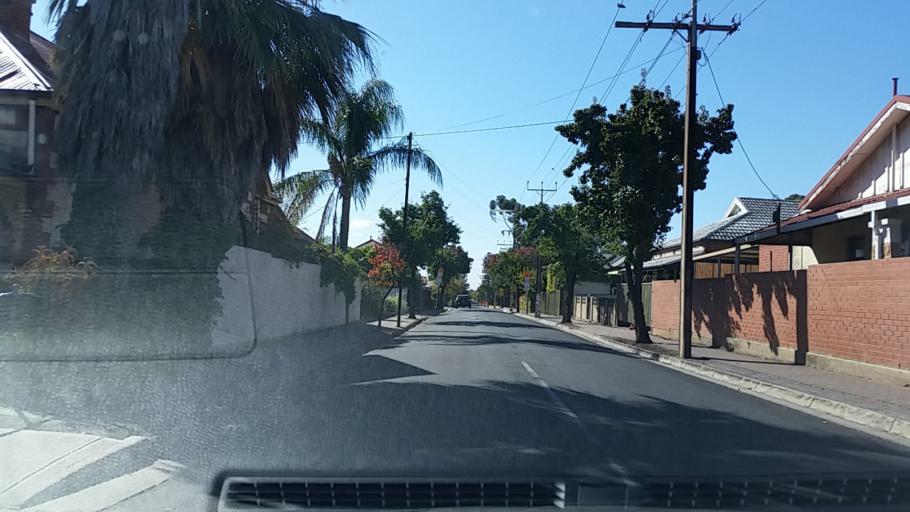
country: AU
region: South Australia
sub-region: Prospect
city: Prospect
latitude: -34.8866
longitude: 138.5895
